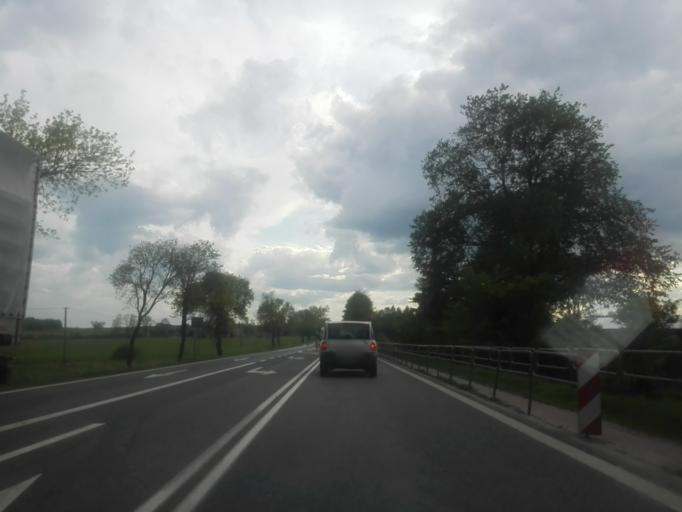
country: PL
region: Podlasie
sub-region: Powiat zambrowski
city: Szumowo
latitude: 52.8732
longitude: 22.0259
